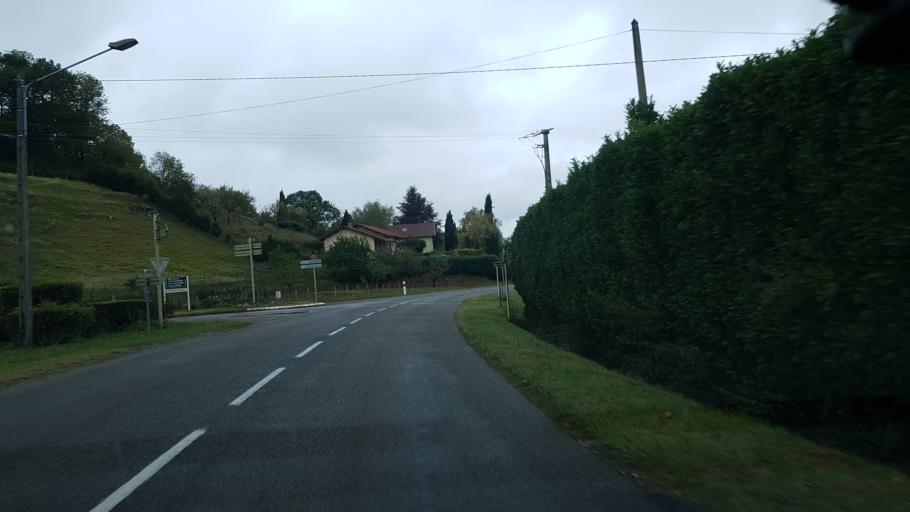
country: FR
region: Rhone-Alpes
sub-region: Departement de l'Ain
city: Tossiat
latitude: 46.1441
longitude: 5.3260
